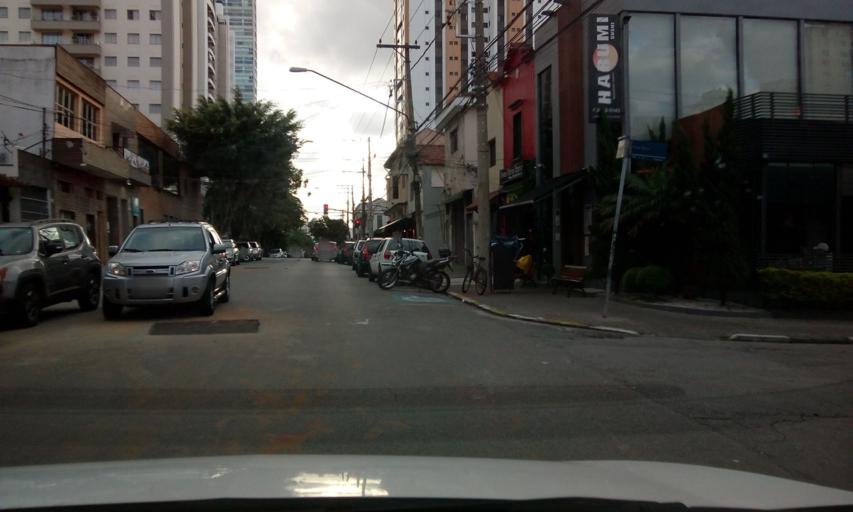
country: BR
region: Sao Paulo
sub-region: Sao Paulo
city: Sao Paulo
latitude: -23.5460
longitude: -46.5681
